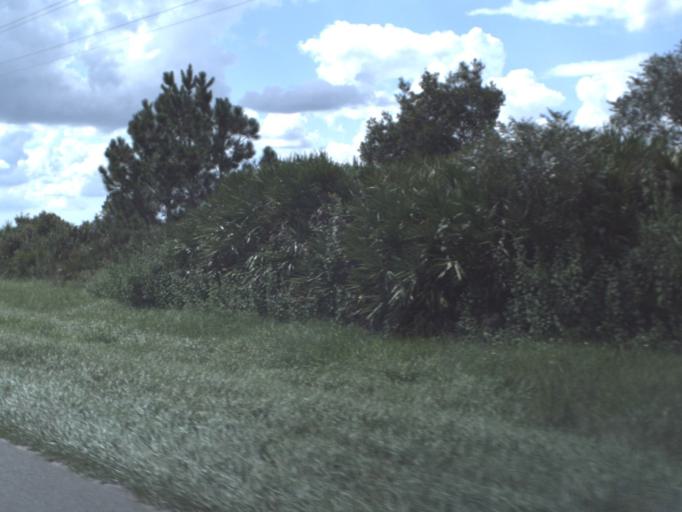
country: US
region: Florida
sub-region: Hillsborough County
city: Wimauma
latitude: 27.5850
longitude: -82.1706
